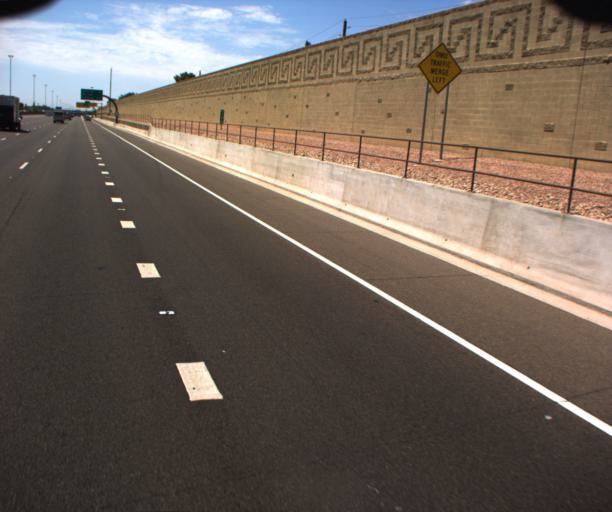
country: US
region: Arizona
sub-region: Maricopa County
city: Tempe
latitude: 33.3859
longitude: -111.9158
